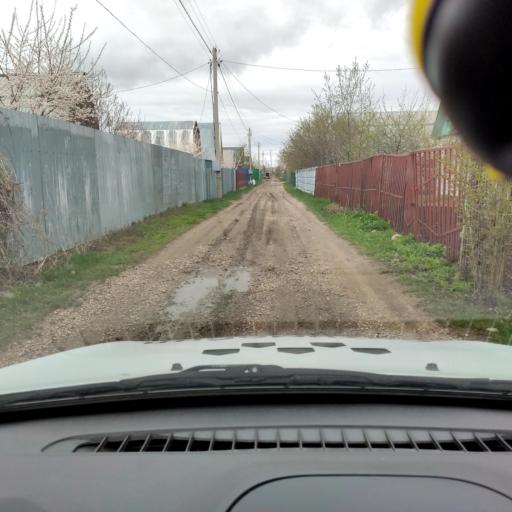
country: RU
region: Samara
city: Tol'yatti
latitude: 53.5835
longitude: 49.3160
